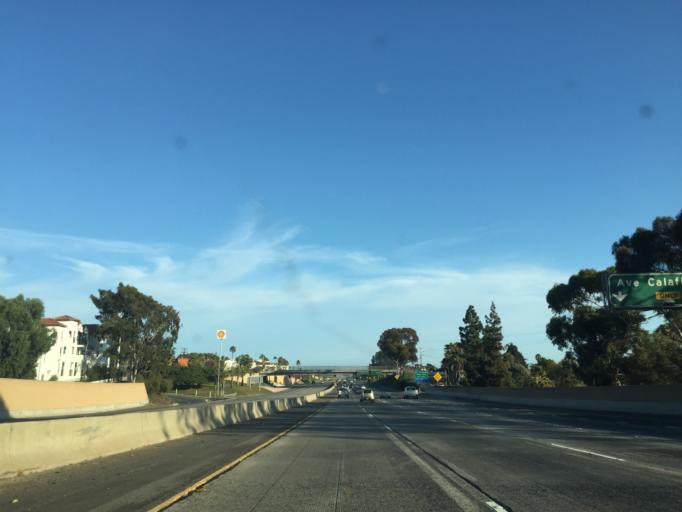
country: US
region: California
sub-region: Orange County
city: San Clemente
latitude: 33.4145
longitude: -117.6029
